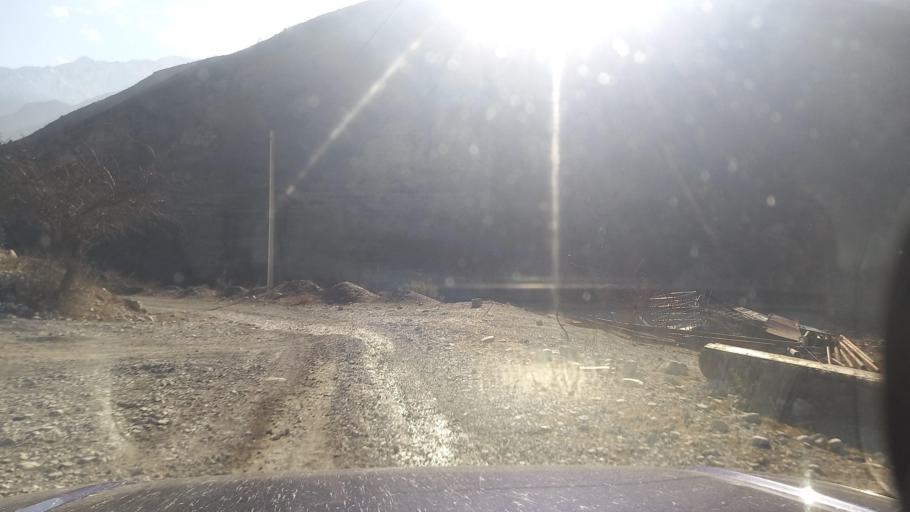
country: RU
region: Ingushetiya
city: Dzhayrakh
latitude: 42.8438
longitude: 44.6515
